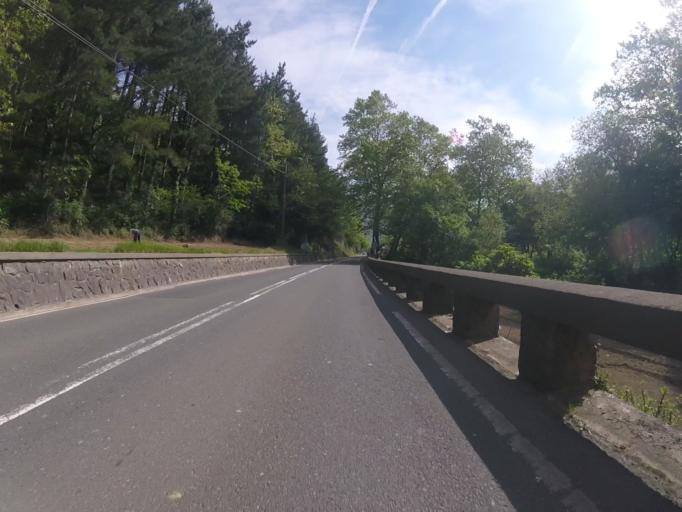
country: ES
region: Basque Country
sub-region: Provincia de Guipuzcoa
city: Azkoitia
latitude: 43.1690
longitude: -2.3271
